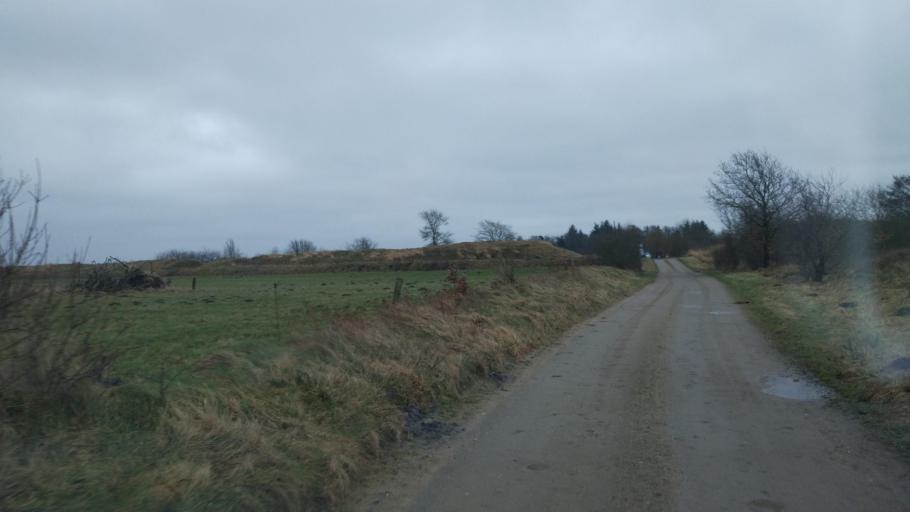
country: DE
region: Schleswig-Holstein
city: Gross Rheide
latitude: 54.4590
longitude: 9.4330
